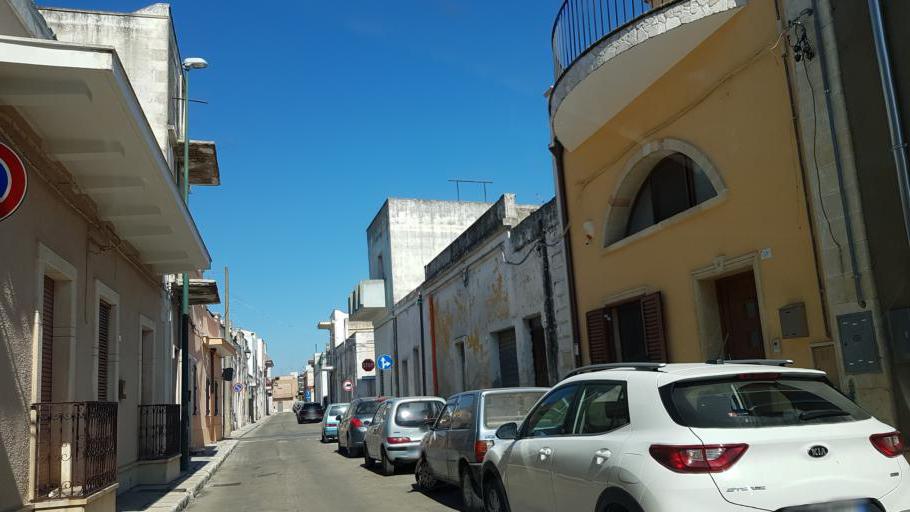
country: IT
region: Apulia
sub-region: Provincia di Brindisi
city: San Pancrazio Salentino
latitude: 40.4177
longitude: 17.8363
